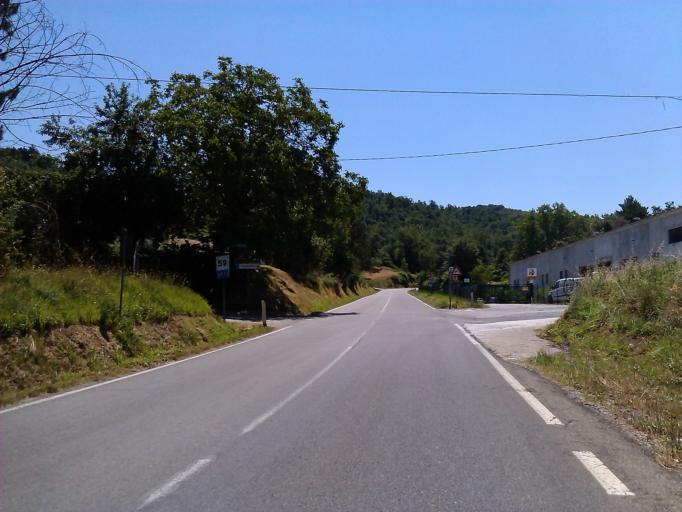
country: IT
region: Umbria
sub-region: Provincia di Terni
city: Fabro Scalo
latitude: 42.8649
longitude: 12.0499
